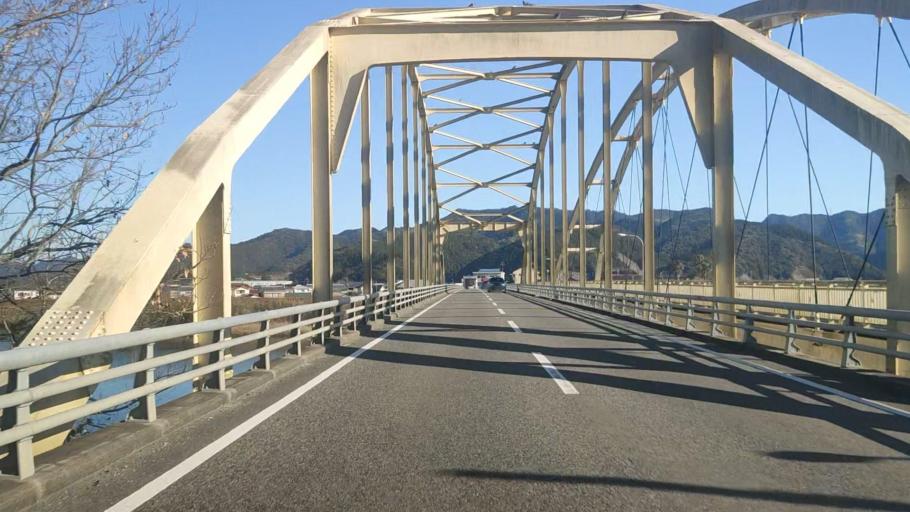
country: JP
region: Miyazaki
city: Nobeoka
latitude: 32.6122
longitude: 131.6890
